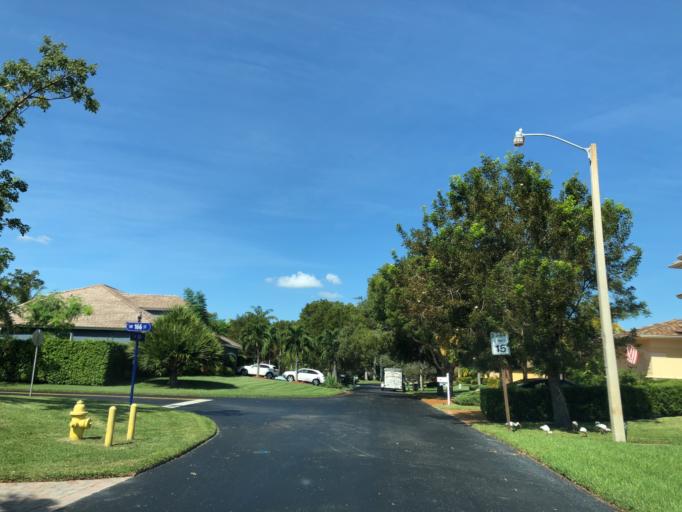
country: US
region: Florida
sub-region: Miami-Dade County
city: Palmetto Bay
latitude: 25.6161
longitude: -80.3306
